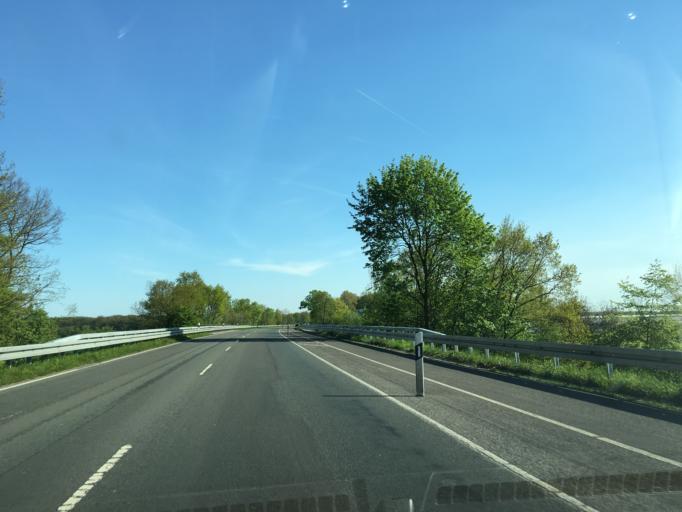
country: DE
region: North Rhine-Westphalia
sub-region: Regierungsbezirk Munster
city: Senden
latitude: 51.9084
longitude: 7.4902
